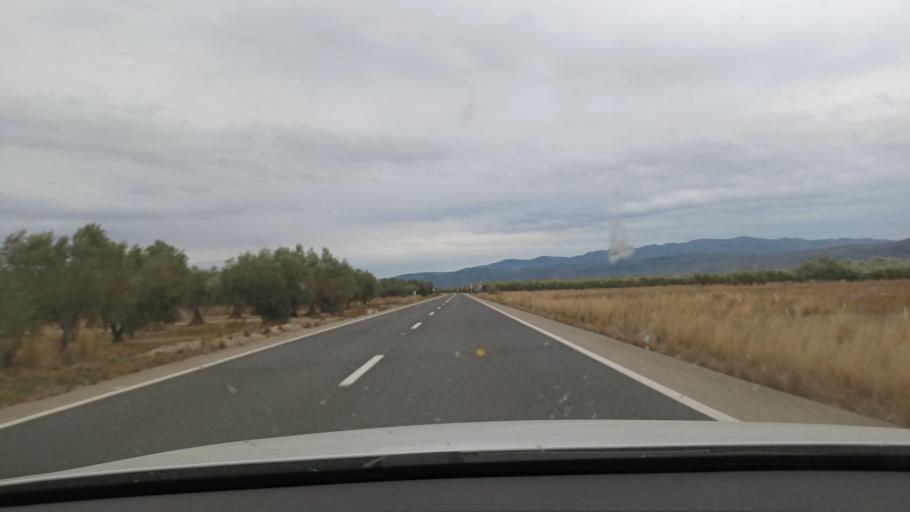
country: ES
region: Catalonia
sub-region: Provincia de Tarragona
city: Ulldecona
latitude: 40.6421
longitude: 0.3686
